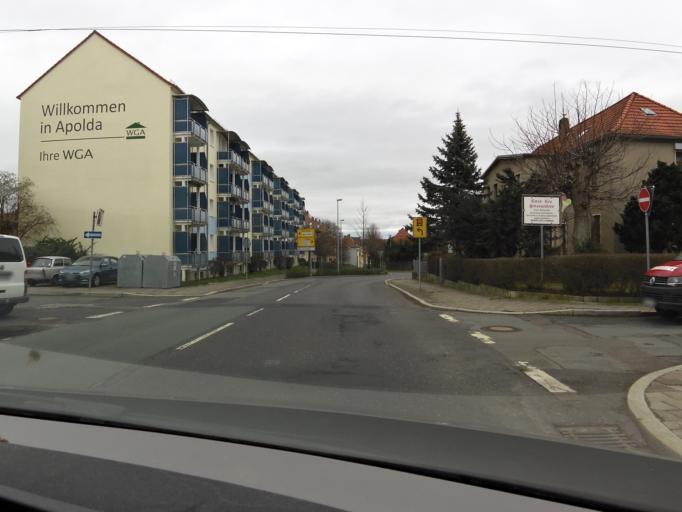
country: DE
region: Thuringia
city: Apolda
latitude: 51.0303
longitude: 11.5032
